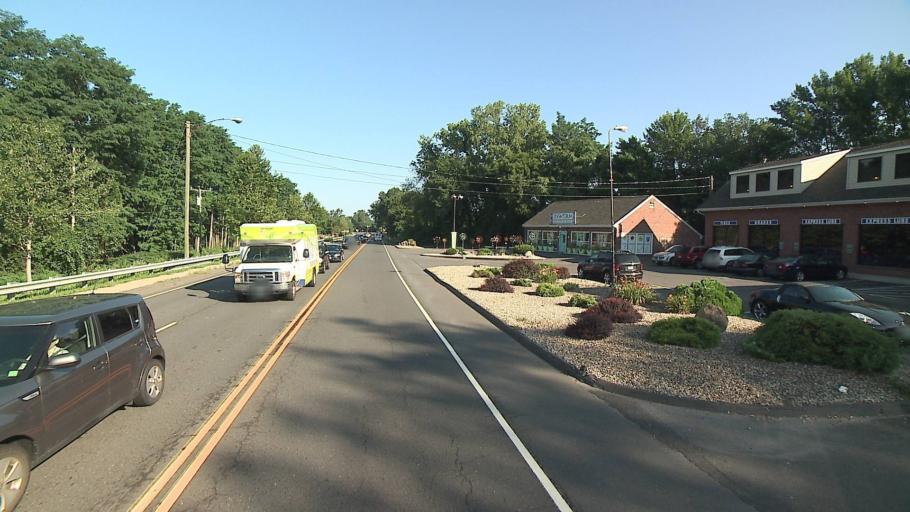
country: US
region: Connecticut
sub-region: Hartford County
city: Farmington
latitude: 41.7297
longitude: -72.8295
